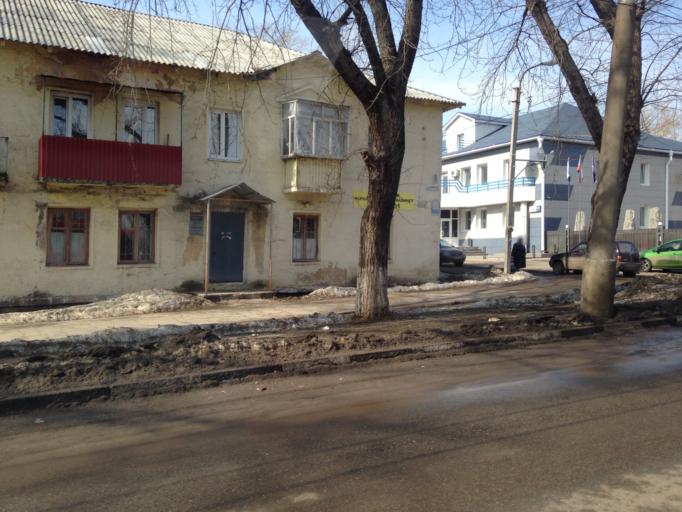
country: RU
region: Ulyanovsk
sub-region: Ulyanovskiy Rayon
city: Ulyanovsk
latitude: 54.3397
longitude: 48.5493
